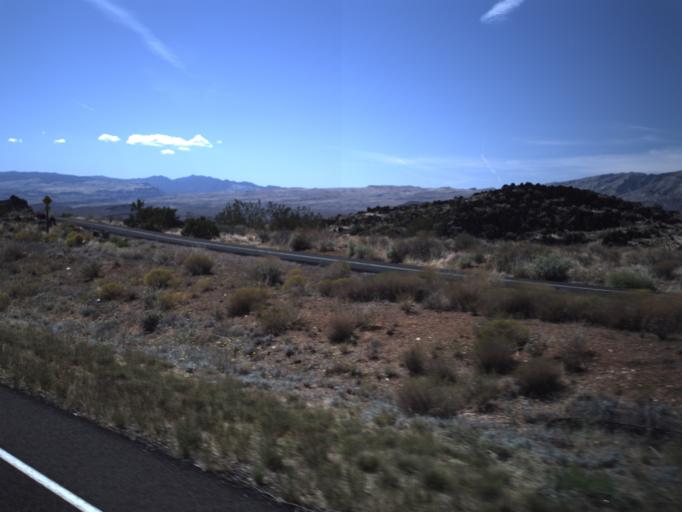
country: US
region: Utah
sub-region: Washington County
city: Santa Clara
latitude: 37.1790
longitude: -113.6191
